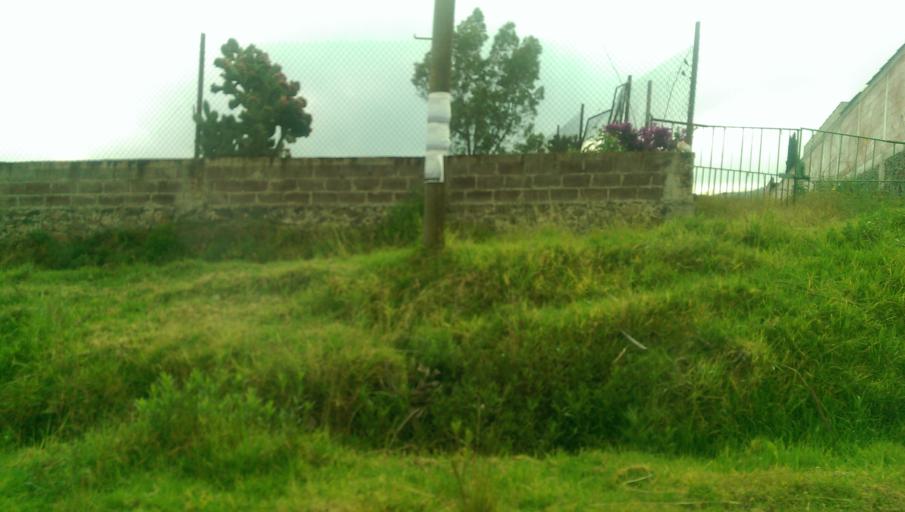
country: MX
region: Mexico
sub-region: Jilotepec
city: Jilotepec de Molina Enriquez
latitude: 19.9362
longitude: -99.4922
